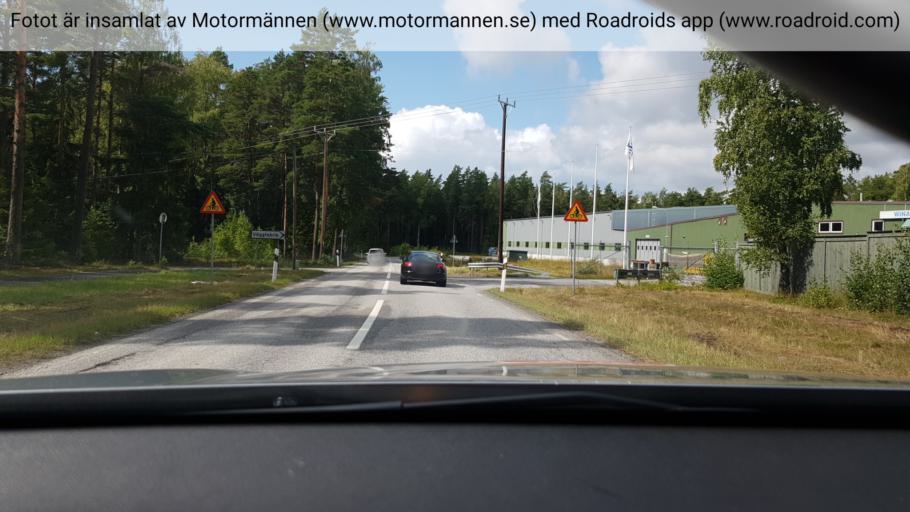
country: SE
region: Stockholm
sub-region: Ekero Kommun
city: Ekeroe
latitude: 59.2804
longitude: 17.7541
